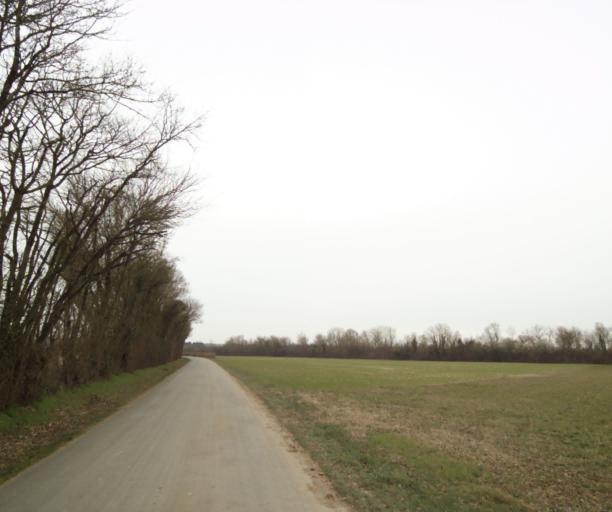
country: FR
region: Poitou-Charentes
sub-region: Departement des Deux-Sevres
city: Magne
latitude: 46.3287
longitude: -0.5282
